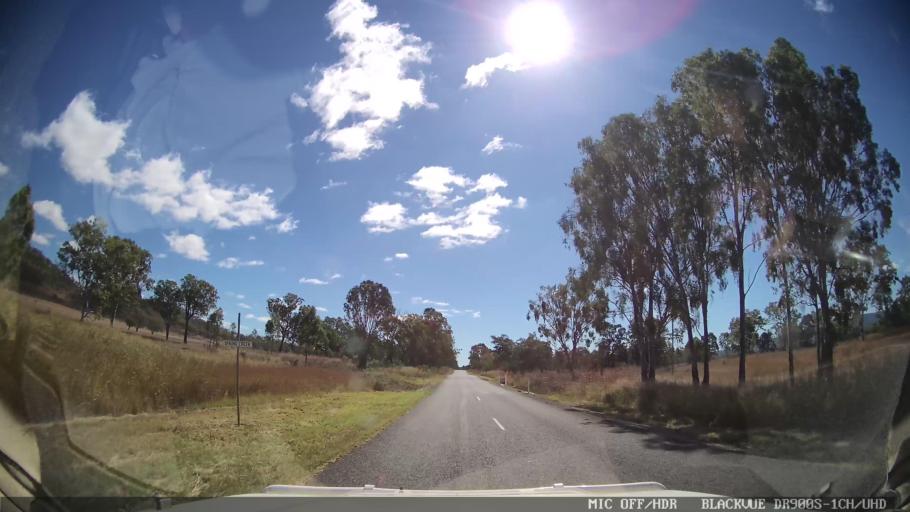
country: AU
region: Queensland
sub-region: Gladstone
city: Toolooa
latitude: -24.4472
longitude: 151.3435
